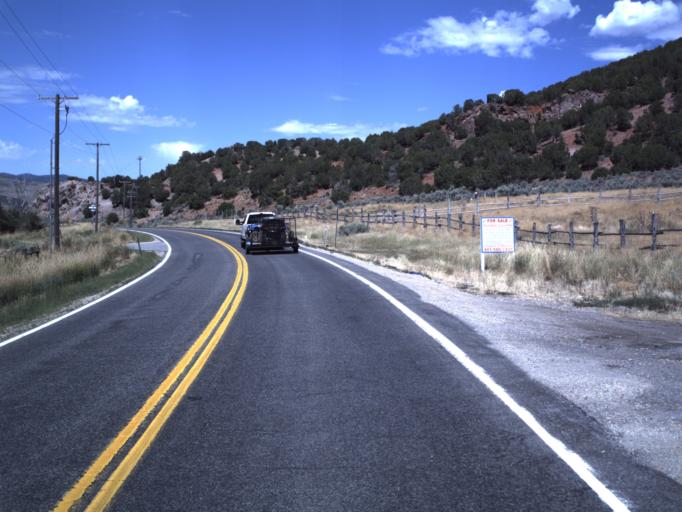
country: US
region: Utah
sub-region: Summit County
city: Oakley
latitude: 40.7405
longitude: -111.3524
